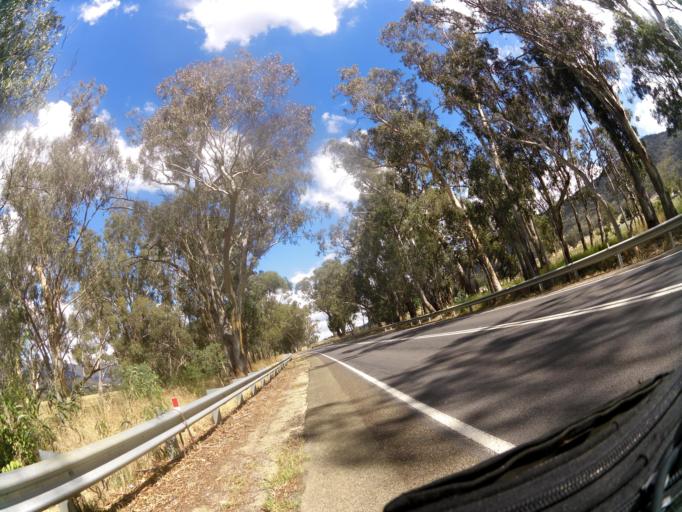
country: AU
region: Victoria
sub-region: Benalla
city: Benalla
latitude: -36.8061
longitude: 146.0070
